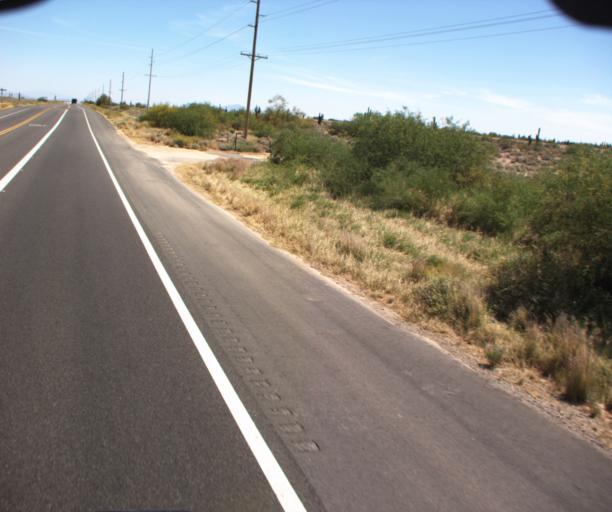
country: US
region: Arizona
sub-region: Pinal County
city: Blackwater
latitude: 33.0301
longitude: -111.6476
